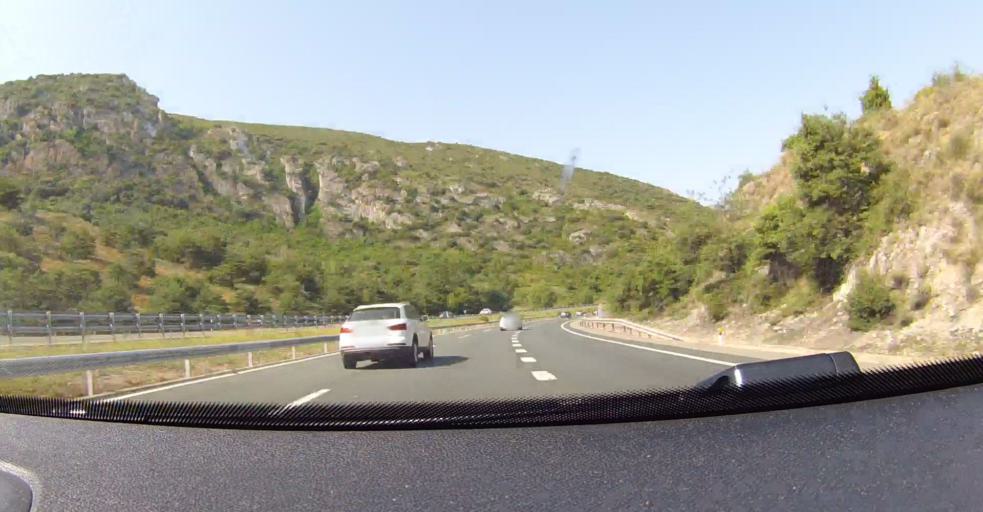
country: ES
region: Castille and Leon
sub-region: Provincia de Burgos
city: Ameyugo
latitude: 42.6464
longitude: -3.0835
